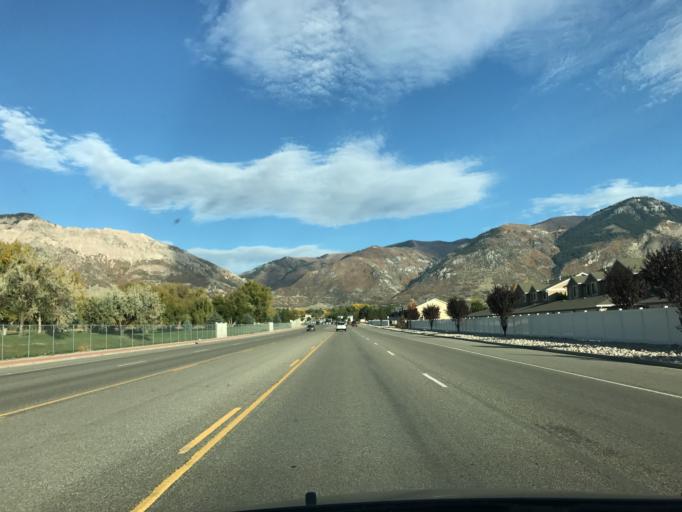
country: US
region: Utah
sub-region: Weber County
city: Pleasant View
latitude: 41.3056
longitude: -111.9839
